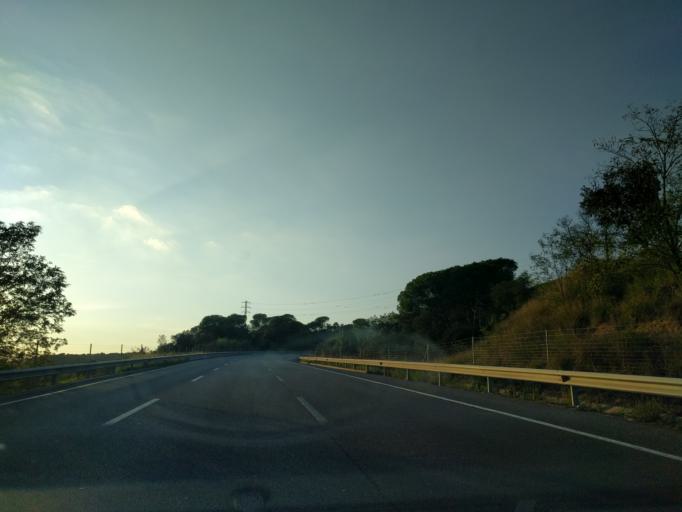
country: ES
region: Catalonia
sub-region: Provincia de Girona
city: Llagostera
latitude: 41.8286
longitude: 2.9401
